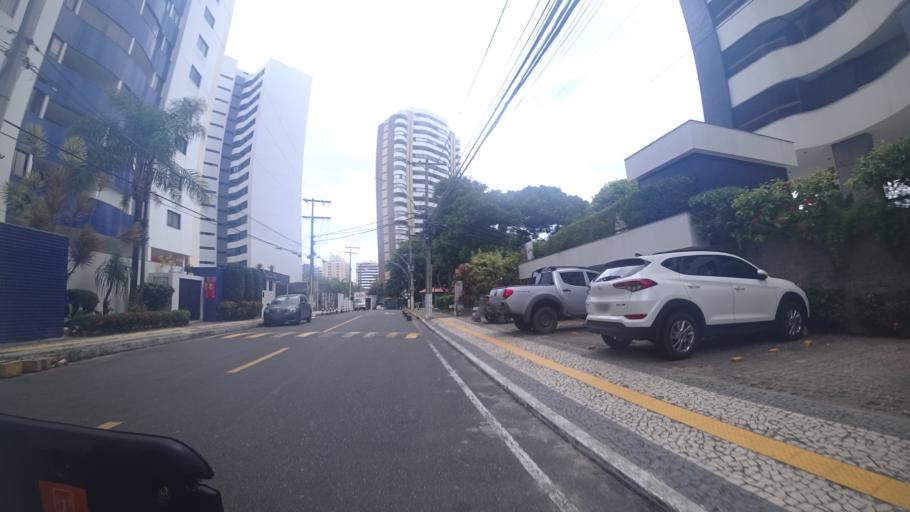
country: BR
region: Bahia
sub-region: Salvador
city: Salvador
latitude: -12.9997
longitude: -38.4673
